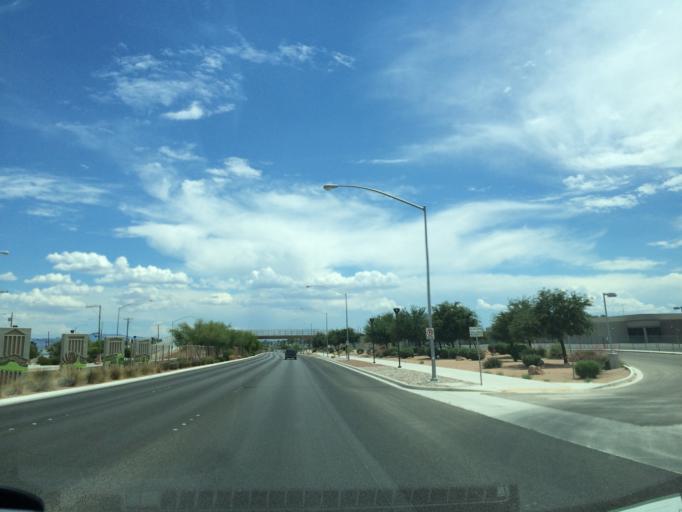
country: US
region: Nevada
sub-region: Clark County
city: North Las Vegas
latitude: 36.2019
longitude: -115.1339
